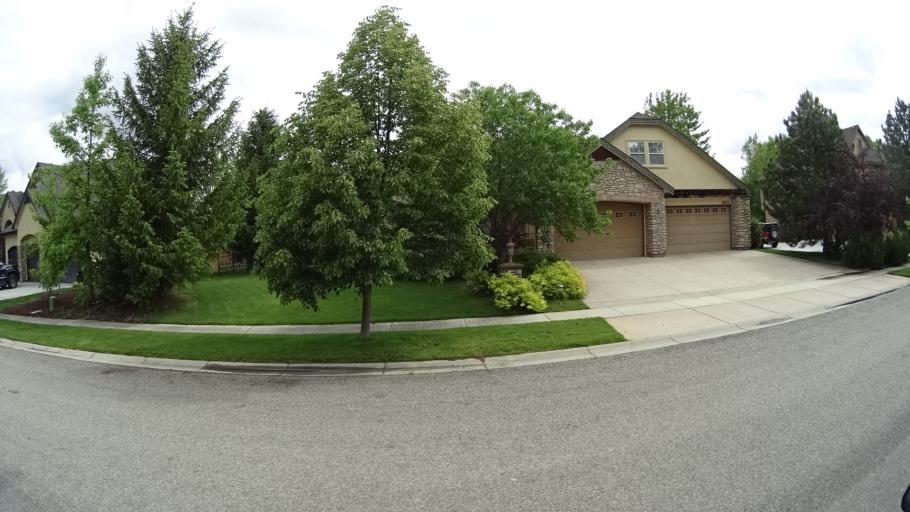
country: US
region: Idaho
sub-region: Ada County
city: Eagle
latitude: 43.6803
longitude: -116.3623
